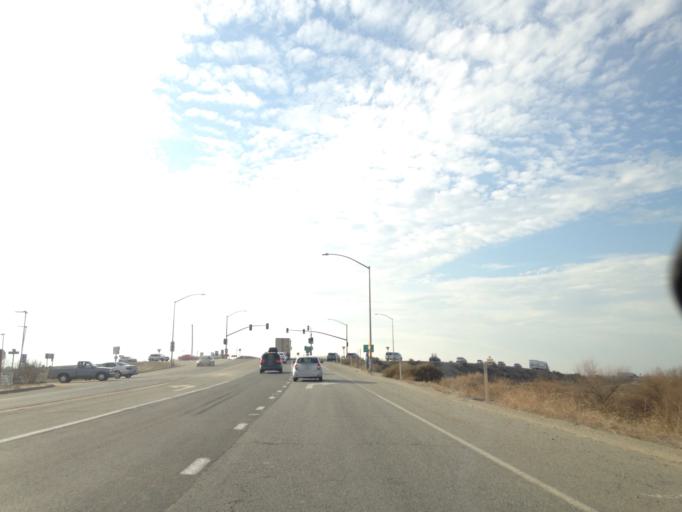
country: US
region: California
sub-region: Kern County
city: Lost Hills
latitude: 35.6164
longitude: -119.6493
